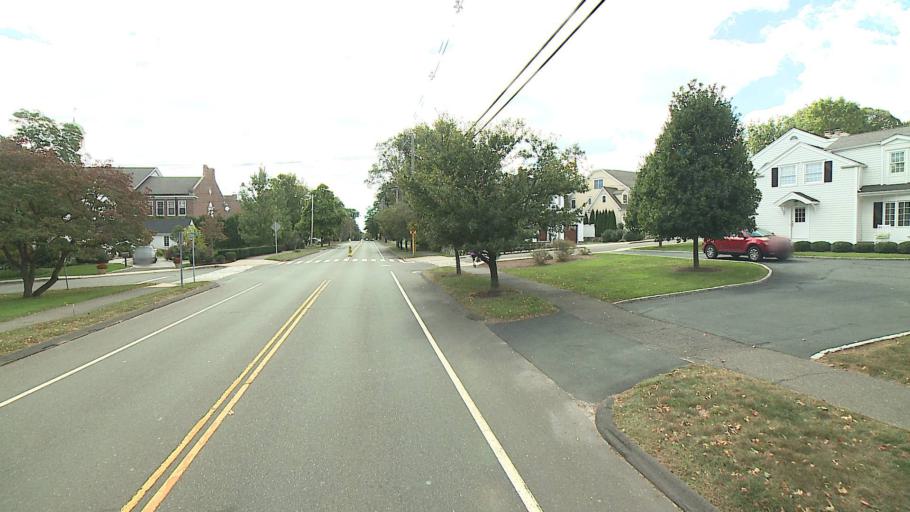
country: US
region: Connecticut
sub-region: Fairfield County
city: New Canaan
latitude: 41.1424
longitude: -73.4919
